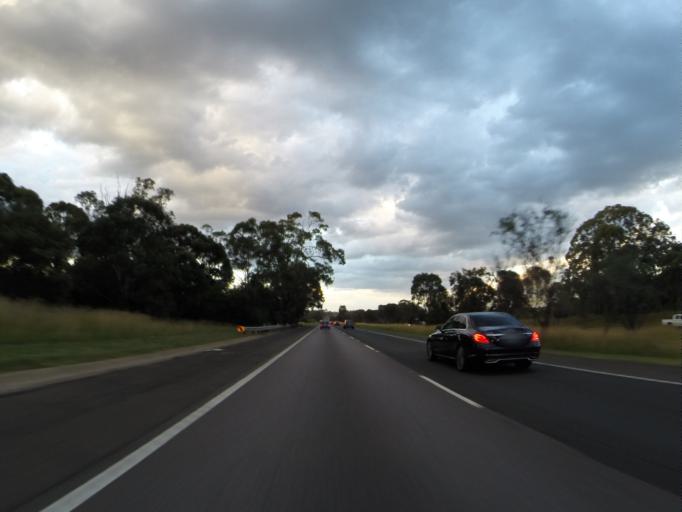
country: AU
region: New South Wales
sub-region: Campbelltown Municipality
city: Glen Alpine
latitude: -34.1053
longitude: 150.7622
